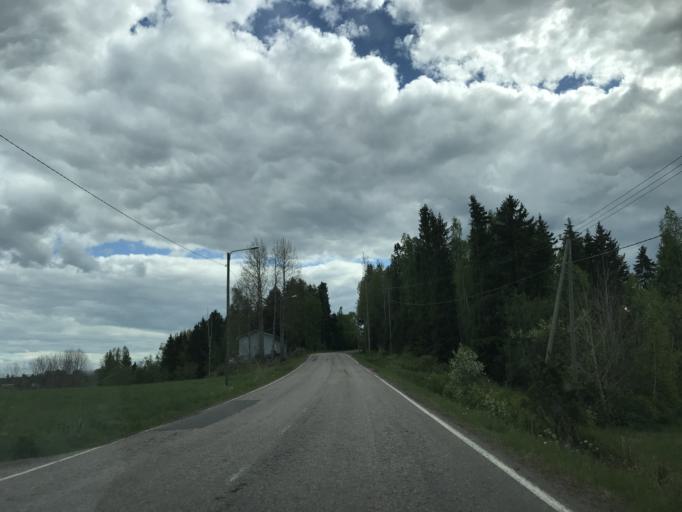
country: FI
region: Uusimaa
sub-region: Helsinki
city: Nurmijaervi
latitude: 60.4279
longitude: 24.7123
